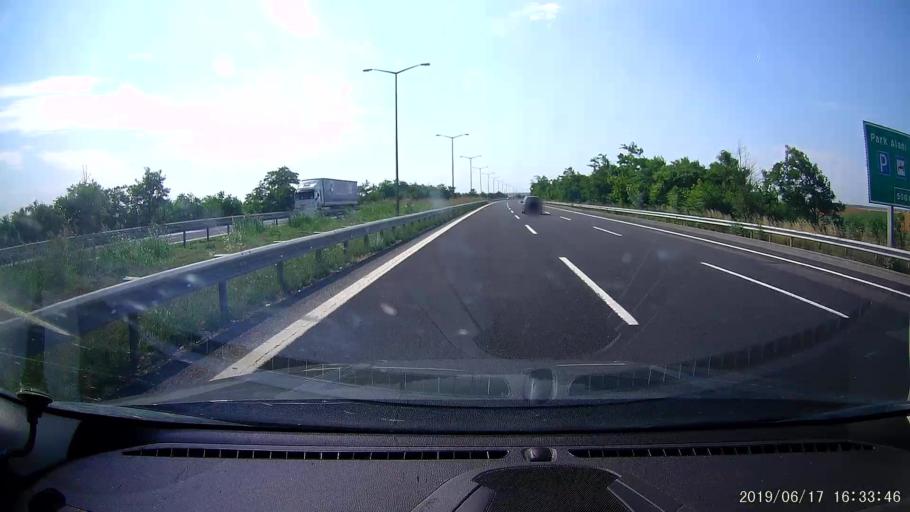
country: TR
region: Kirklareli
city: Buyukkaristiran
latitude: 41.3842
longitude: 27.5625
